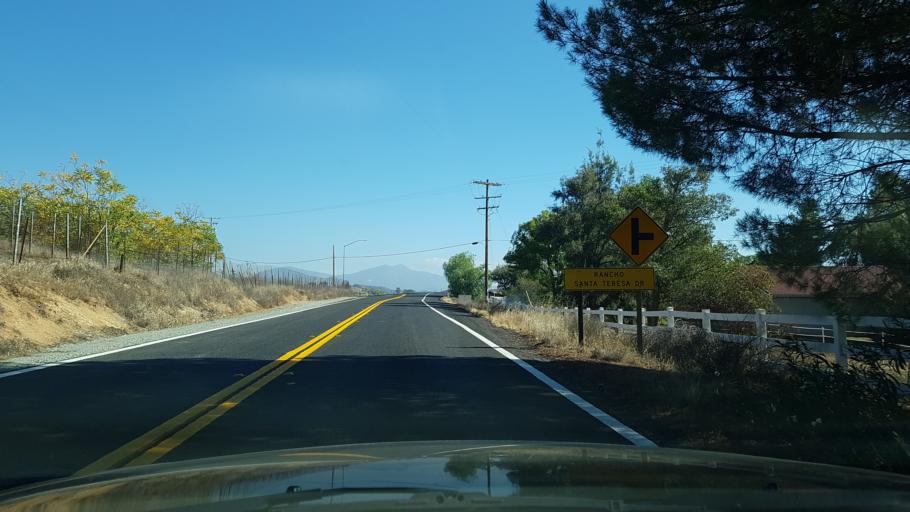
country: US
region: California
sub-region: San Diego County
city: San Diego Country Estates
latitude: 33.0803
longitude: -116.7838
